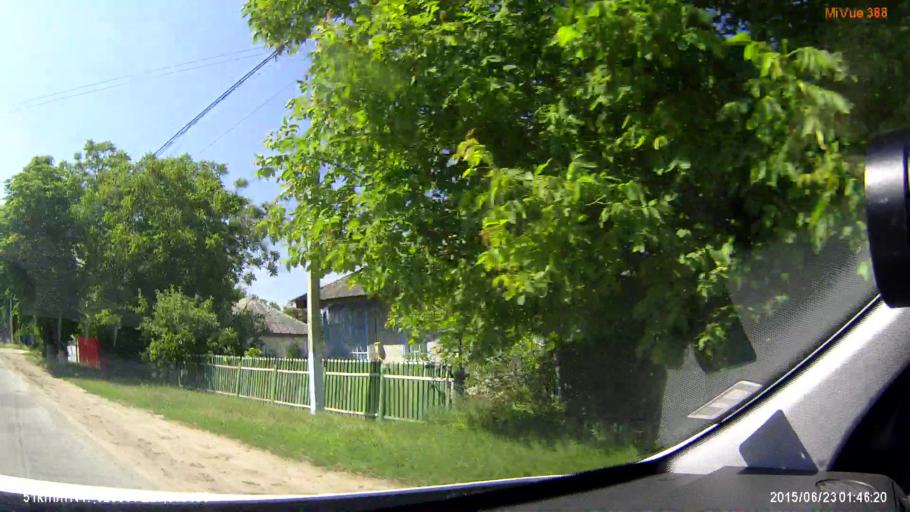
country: RO
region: Iasi
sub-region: Comuna Victoria
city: Victoria
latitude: 47.3250
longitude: 27.6356
